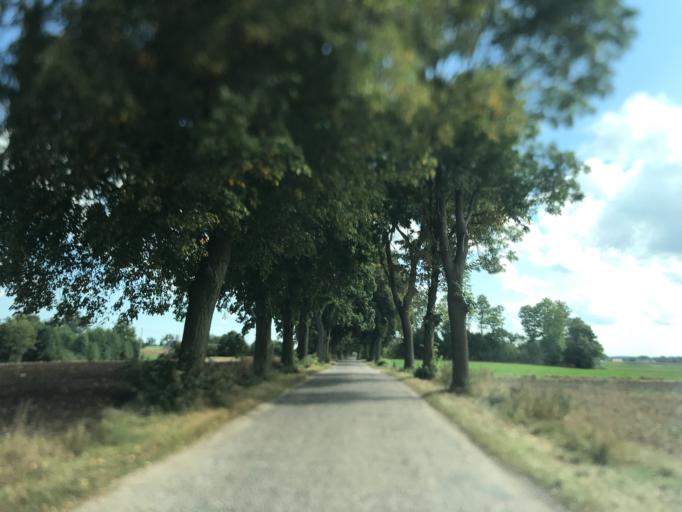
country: PL
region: Kujawsko-Pomorskie
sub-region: Powiat brodnicki
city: Brzozie
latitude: 53.3546
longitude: 19.6801
